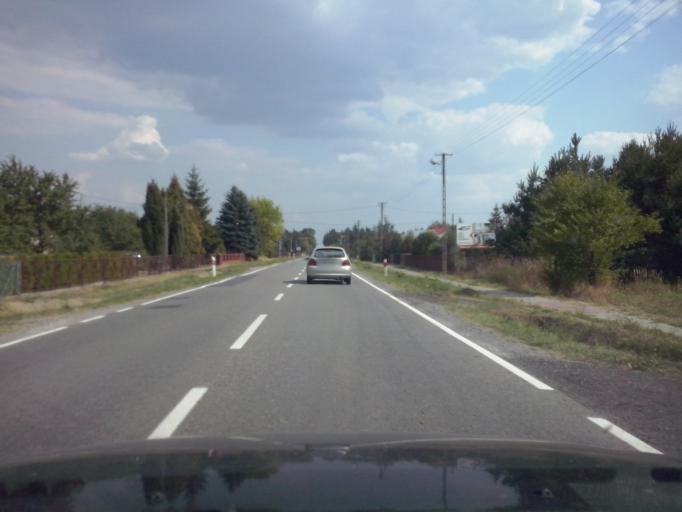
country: PL
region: Subcarpathian Voivodeship
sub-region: Powiat nizanski
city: Raclawice
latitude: 50.4980
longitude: 22.1876
